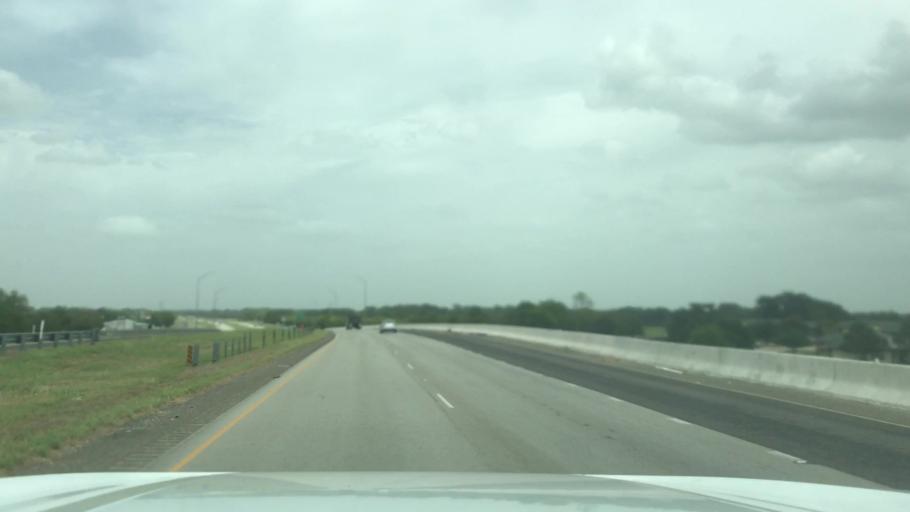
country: US
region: Texas
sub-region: McLennan County
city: Beverly
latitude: 31.5190
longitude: -97.0894
